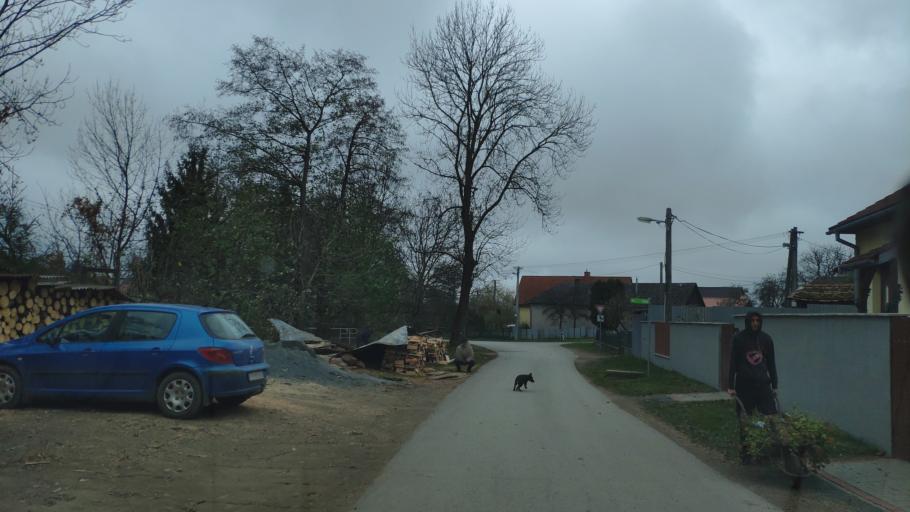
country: SK
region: Presovsky
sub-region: Okres Presov
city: Presov
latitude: 49.1169
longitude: 21.2344
